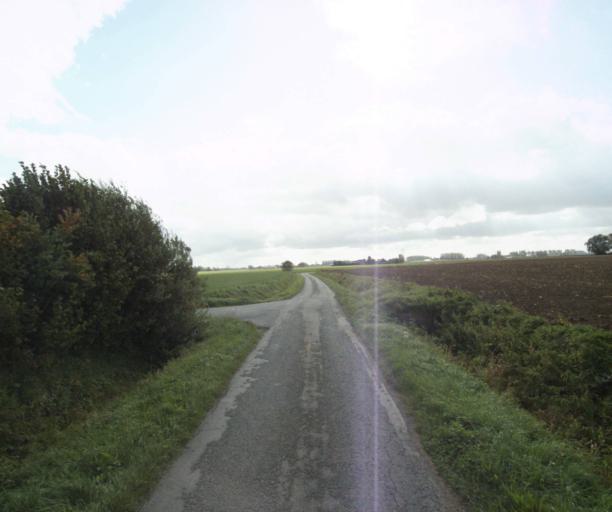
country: FR
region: Nord-Pas-de-Calais
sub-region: Departement du Nord
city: Deulemont
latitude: 50.7214
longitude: 2.9488
